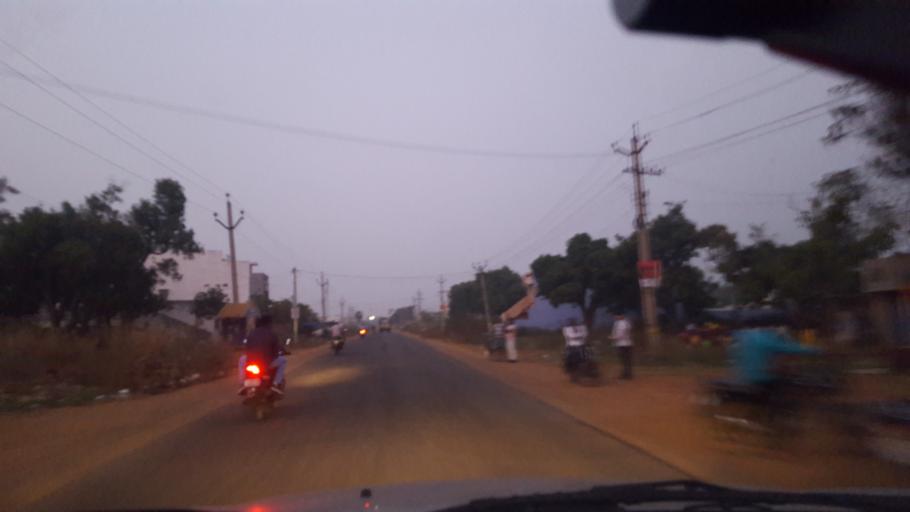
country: IN
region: Andhra Pradesh
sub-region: Srikakulam
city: Palasa
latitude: 18.7485
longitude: 84.4156
